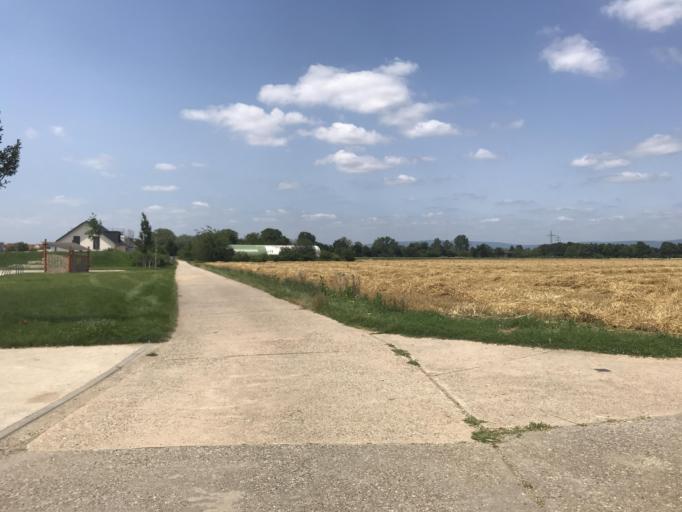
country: DE
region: Hesse
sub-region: Regierungsbezirk Darmstadt
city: Hochheim am Main
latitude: 50.0227
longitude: 8.3577
